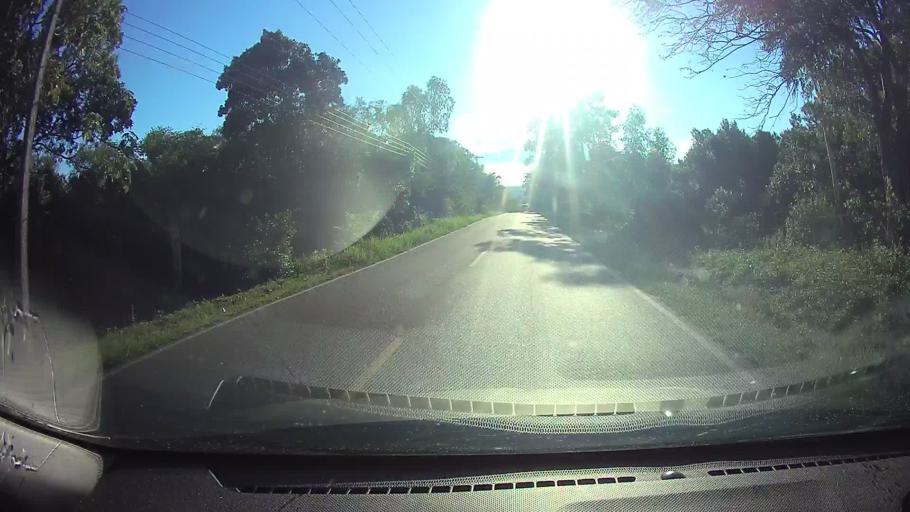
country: PY
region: Cordillera
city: Emboscada
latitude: -25.2015
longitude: -57.3269
